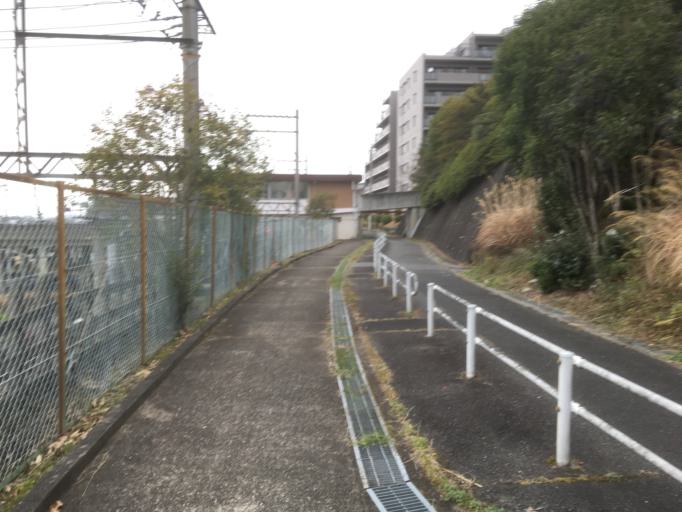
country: JP
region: Nara
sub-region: Ikoma-shi
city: Ikoma
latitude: 34.6561
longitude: 135.7088
